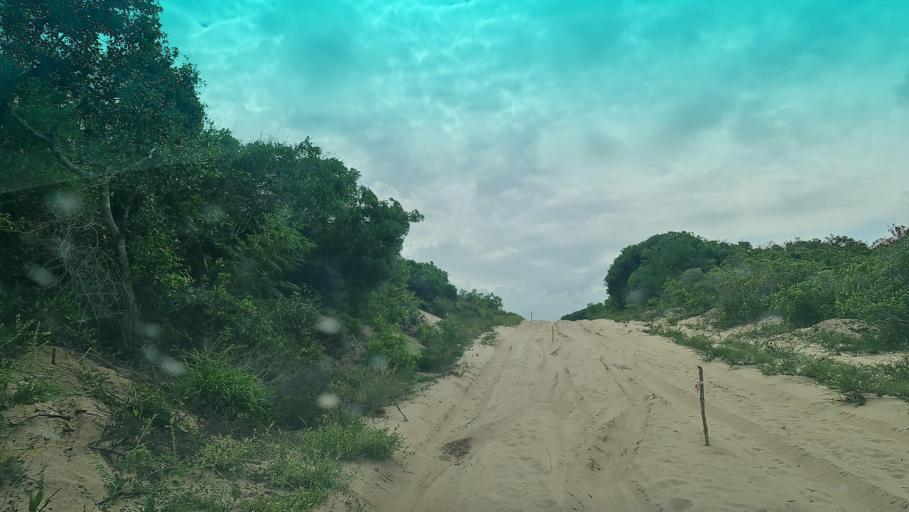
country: MZ
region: Maputo
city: Manhica
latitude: -25.4381
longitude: 32.9197
